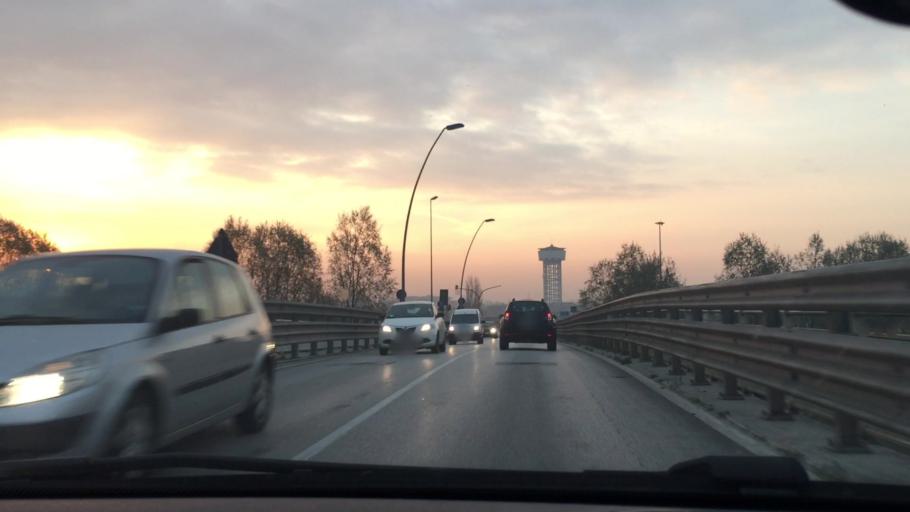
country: IT
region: Veneto
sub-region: Provincia di Venezia
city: Cavarzere
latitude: 45.1406
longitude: 12.0702
